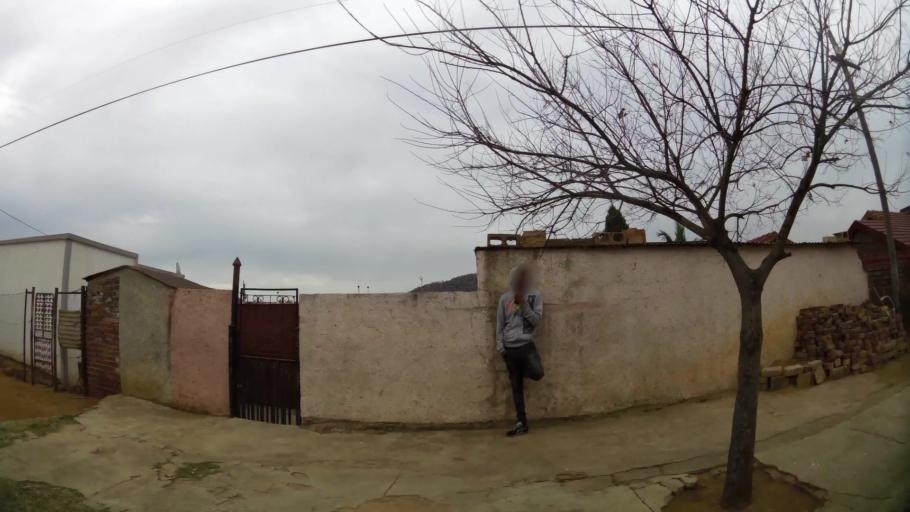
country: ZA
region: Gauteng
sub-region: City of Tshwane Metropolitan Municipality
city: Cullinan
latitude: -25.7079
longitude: 28.3589
